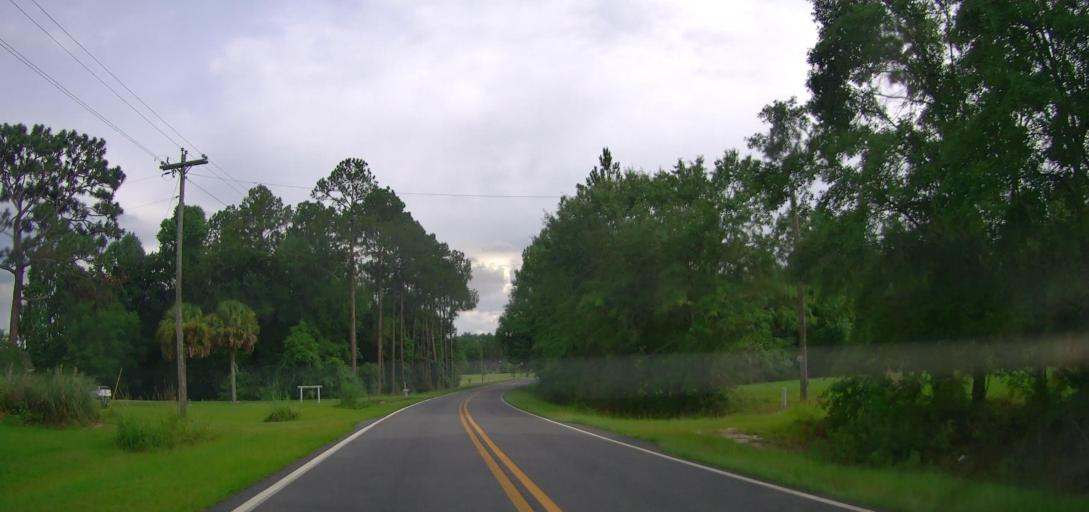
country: US
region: Georgia
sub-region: Wayne County
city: Jesup
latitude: 31.6756
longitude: -81.9181
